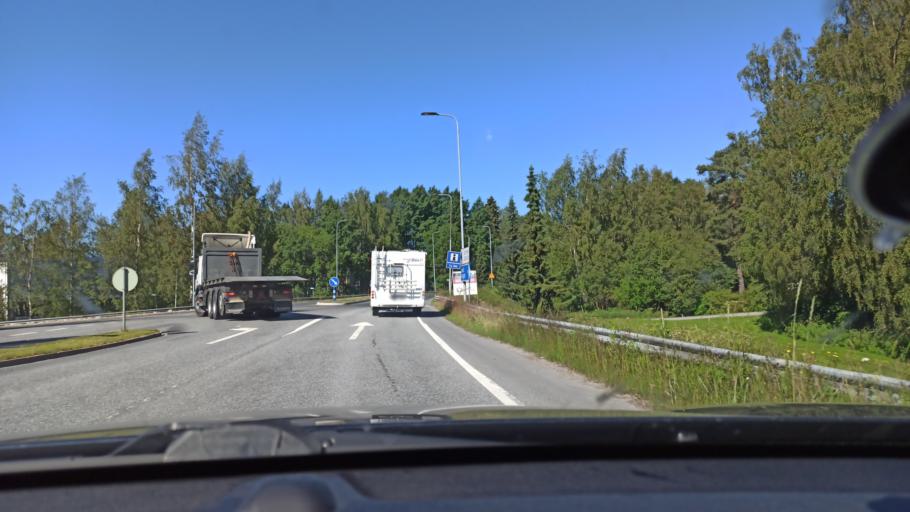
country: FI
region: Ostrobothnia
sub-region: Jakobstadsregionen
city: Jakobstad
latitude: 63.6668
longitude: 22.7071
